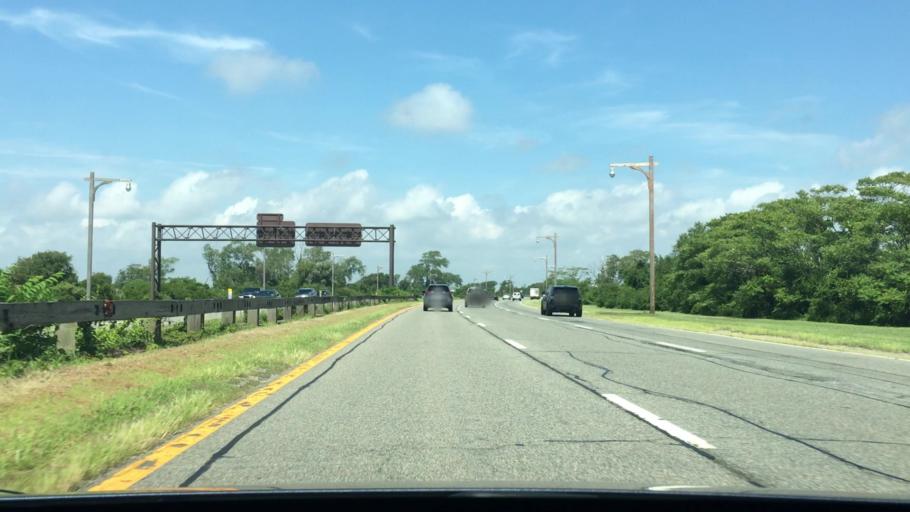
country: US
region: New York
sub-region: Nassau County
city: Point Lookout
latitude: 40.6178
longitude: -73.5574
